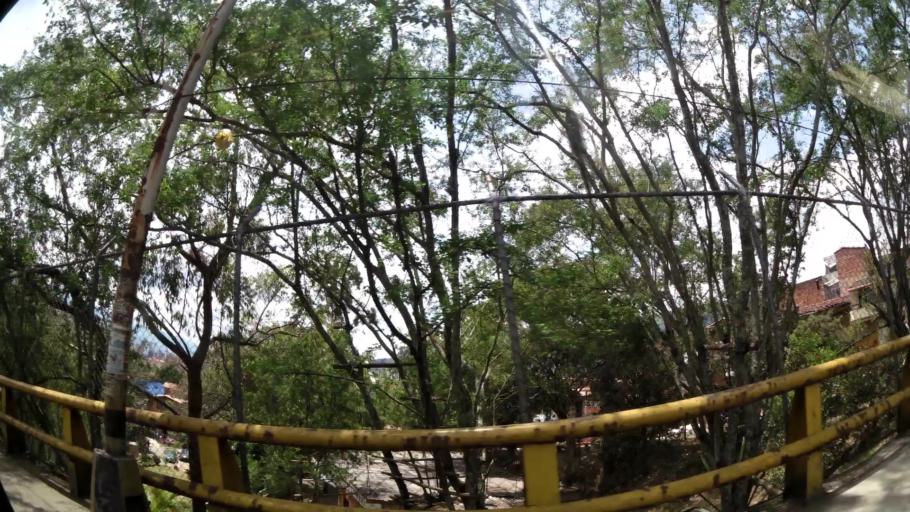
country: CO
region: Antioquia
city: Bello
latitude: 6.3461
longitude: -75.5585
